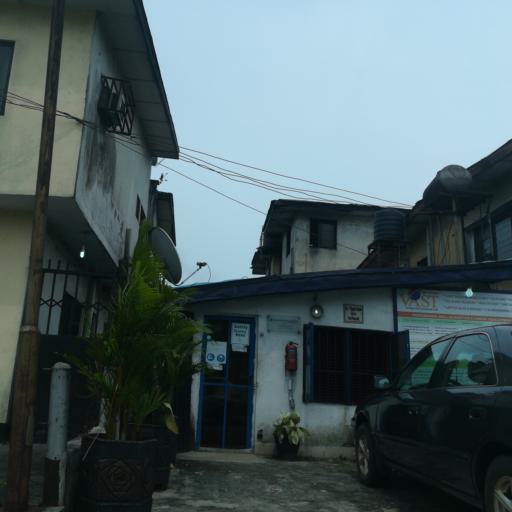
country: NG
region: Rivers
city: Port Harcourt
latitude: 4.7987
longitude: 7.0040
